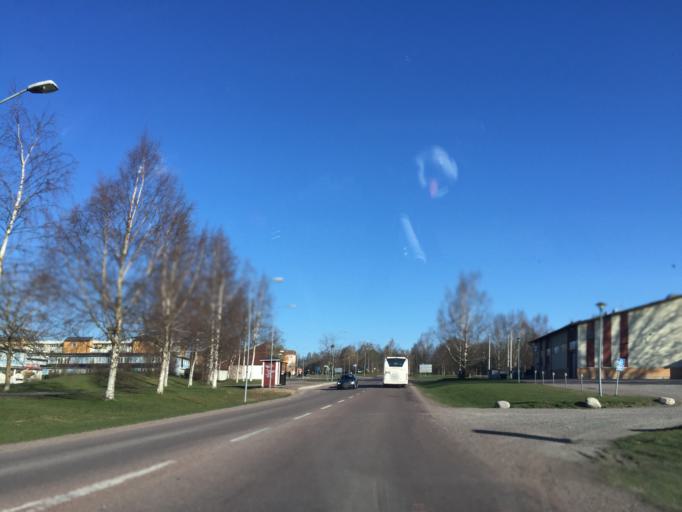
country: SE
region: Dalarna
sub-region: Borlange Kommun
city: Borlaenge
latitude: 60.4825
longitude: 15.4077
